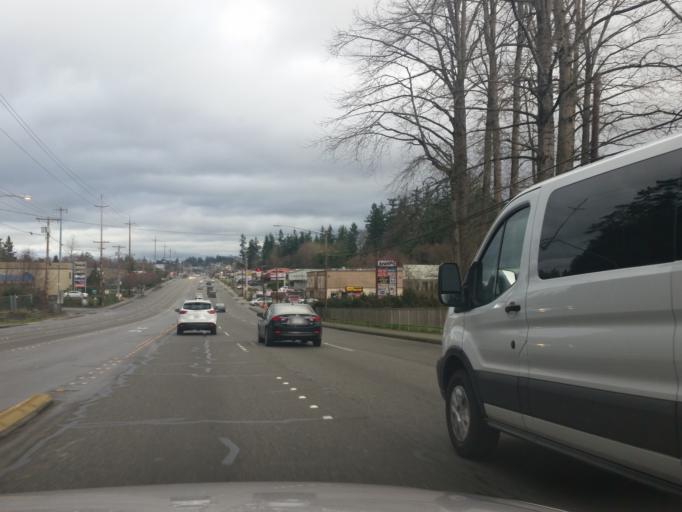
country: US
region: Washington
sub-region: Snohomish County
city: Lynnwood
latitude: 47.8291
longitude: -122.3083
